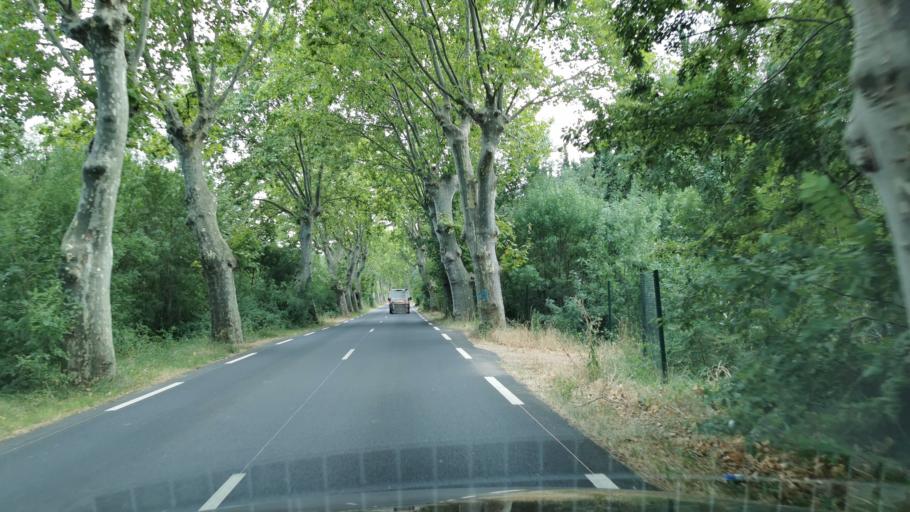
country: FR
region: Languedoc-Roussillon
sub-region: Departement de l'Herault
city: Capestang
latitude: 43.3230
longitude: 3.0362
